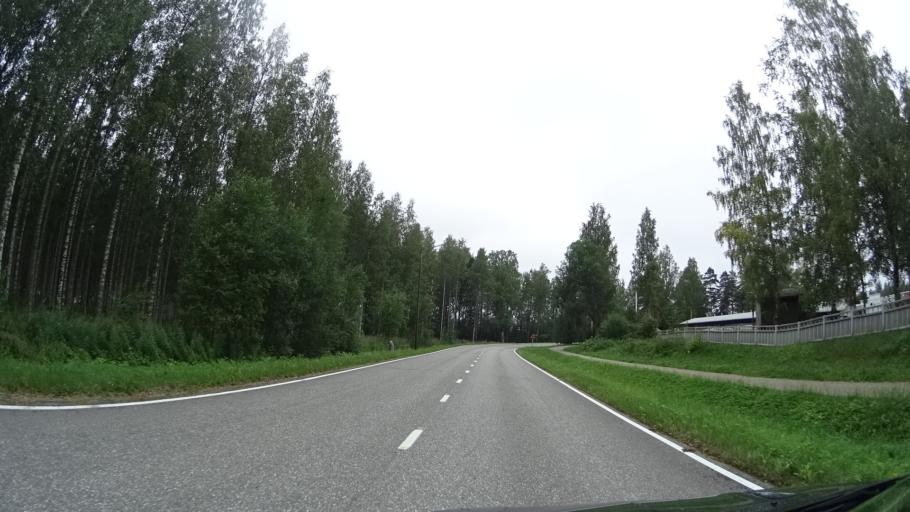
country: FI
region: Southern Savonia
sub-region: Savonlinna
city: Punkaharju
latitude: 61.7538
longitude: 29.3873
